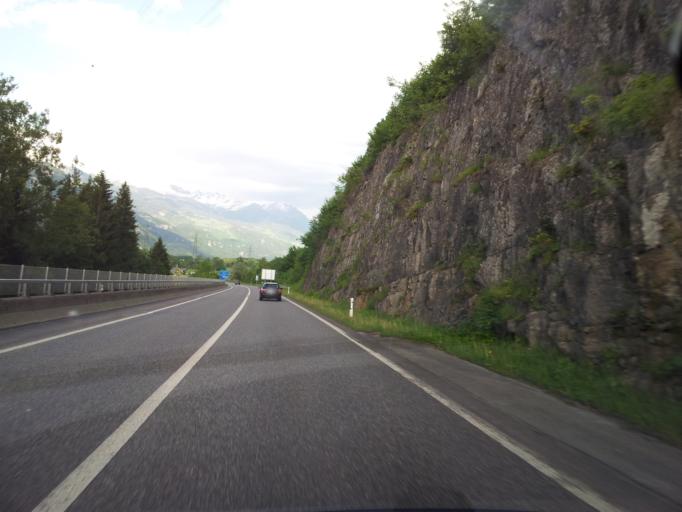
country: CH
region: Bern
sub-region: Interlaken-Oberhasli District
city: Brienz
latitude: 46.7385
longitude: 8.0457
